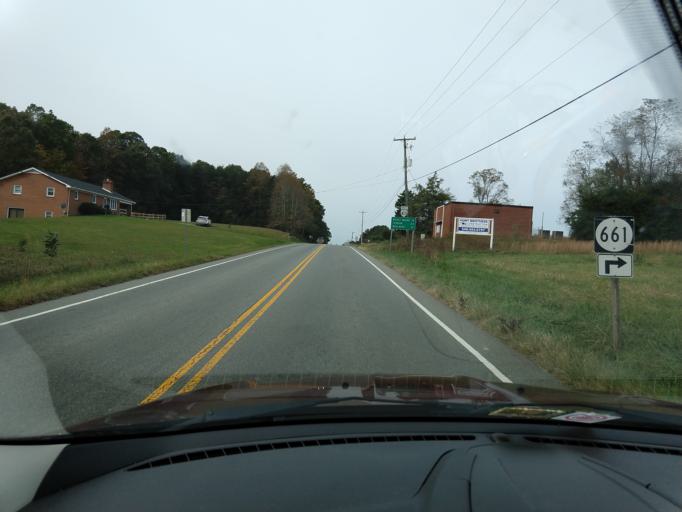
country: US
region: Virginia
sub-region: Franklin County
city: Union Hall
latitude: 36.9972
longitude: -79.6908
